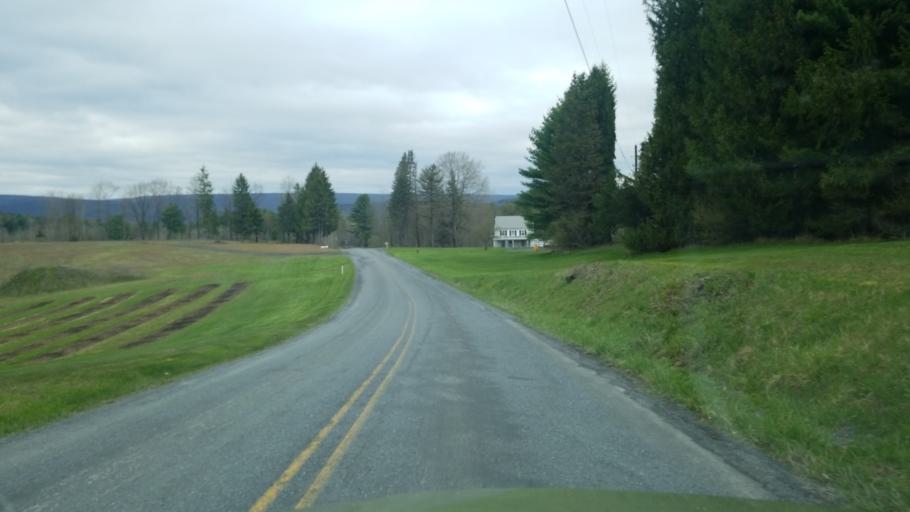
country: US
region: Pennsylvania
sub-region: Clearfield County
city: Clearfield
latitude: 41.0553
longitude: -78.4270
